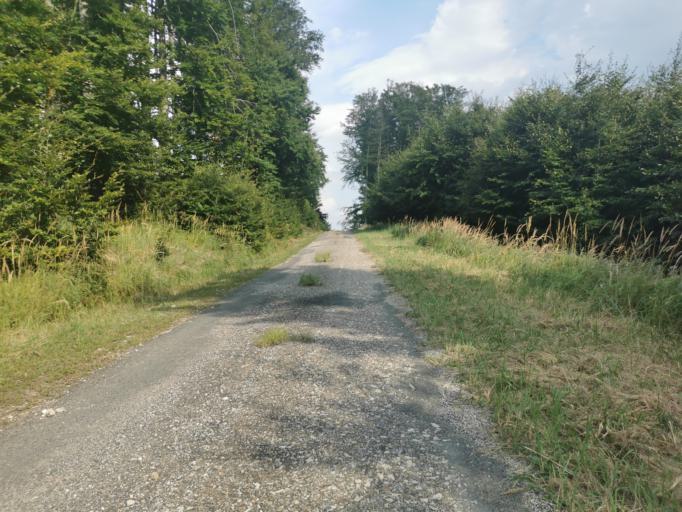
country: SK
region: Nitriansky
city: Stara Tura
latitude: 48.8336
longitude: 17.6290
